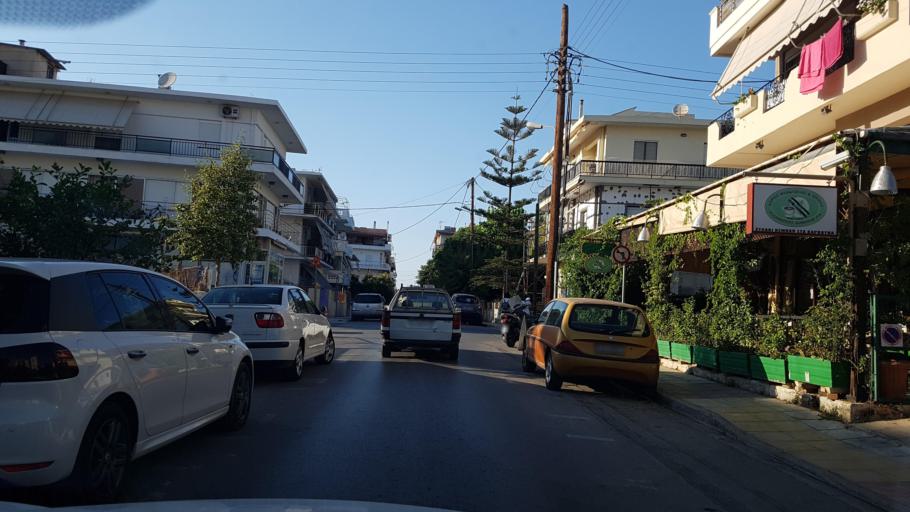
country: GR
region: Crete
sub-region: Nomos Chanias
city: Chania
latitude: 35.5091
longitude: 24.0141
